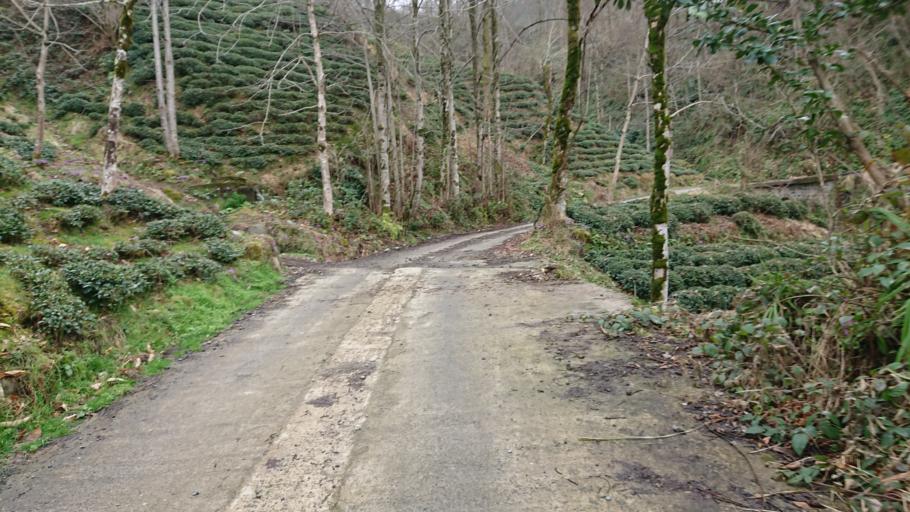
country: TR
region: Rize
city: Rize
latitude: 40.9794
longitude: 40.4963
